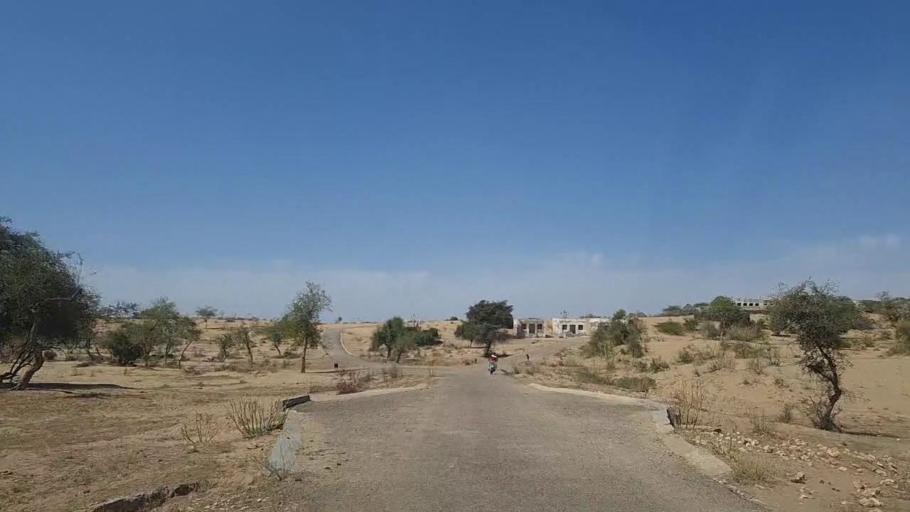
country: PK
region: Sindh
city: Mithi
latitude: 24.8677
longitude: 69.6608
